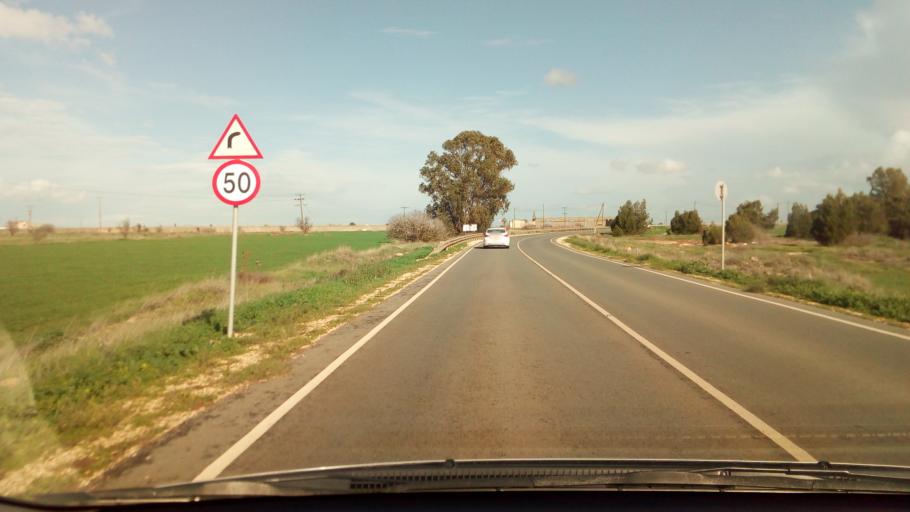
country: CY
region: Ammochostos
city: Achna
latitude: 35.0468
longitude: 33.7722
